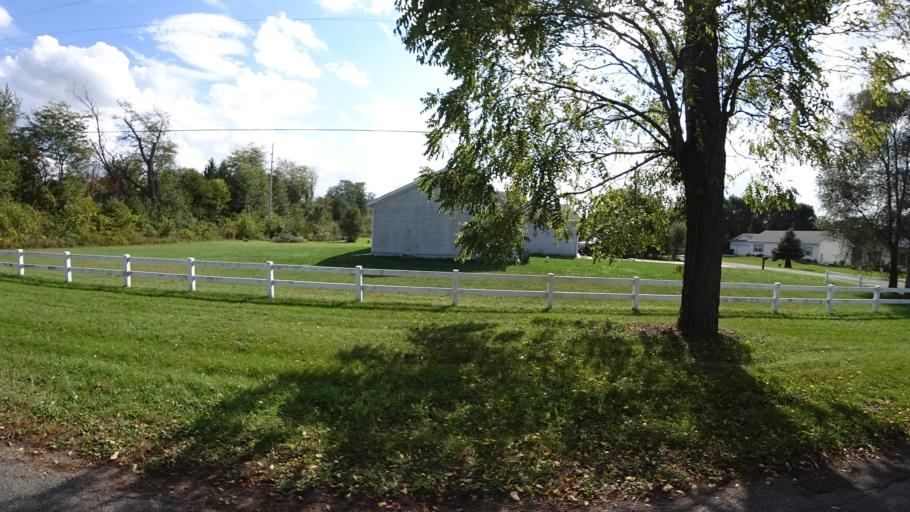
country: US
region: Michigan
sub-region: Saint Joseph County
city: Three Rivers
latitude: 41.9475
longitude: -85.6061
